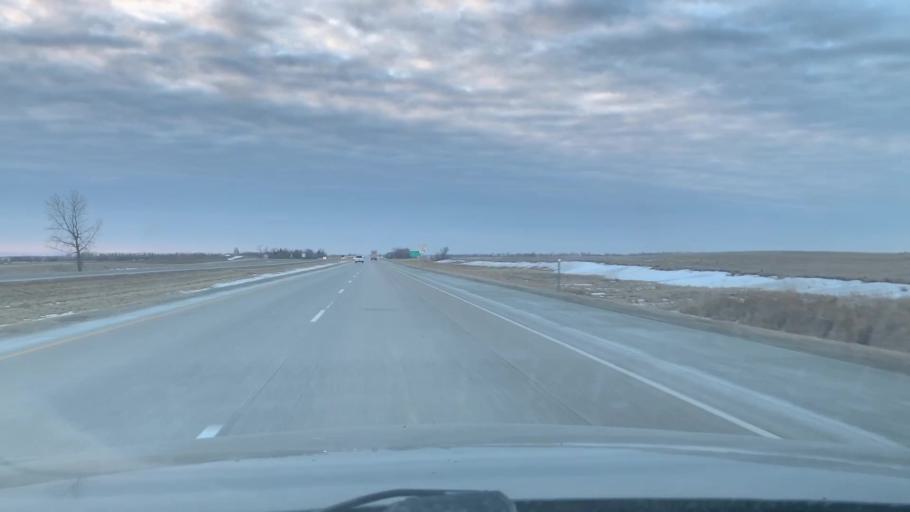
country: US
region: North Dakota
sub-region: Barnes County
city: Valley City
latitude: 46.9202
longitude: -97.6919
